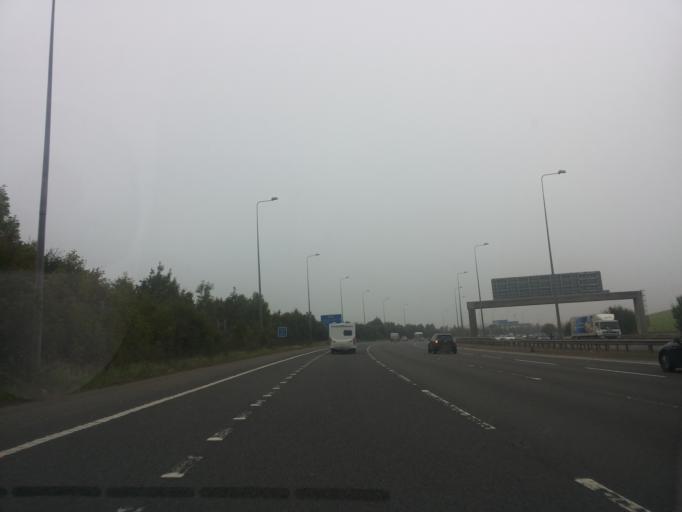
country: GB
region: England
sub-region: Borough of Tameside
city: Droylsden
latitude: 53.4640
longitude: -2.1394
